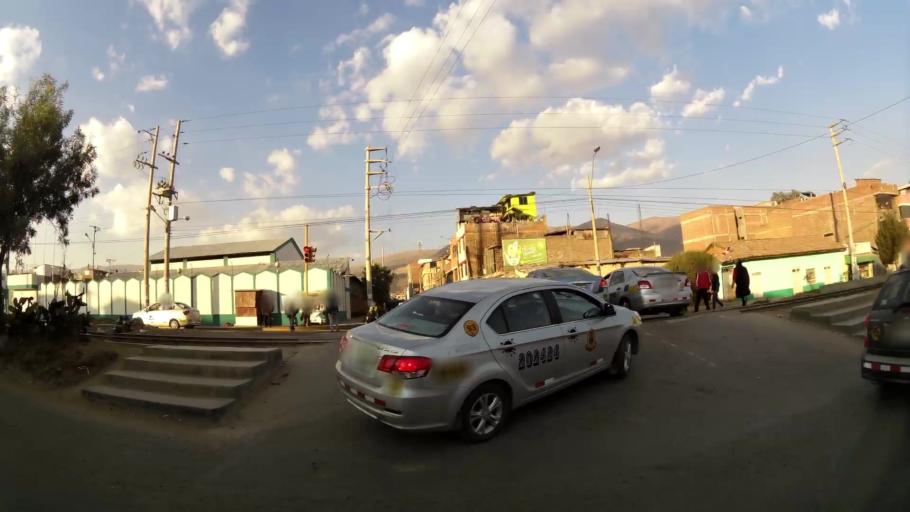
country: PE
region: Junin
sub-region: Provincia de Huancayo
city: El Tambo
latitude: -12.0561
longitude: -75.2125
